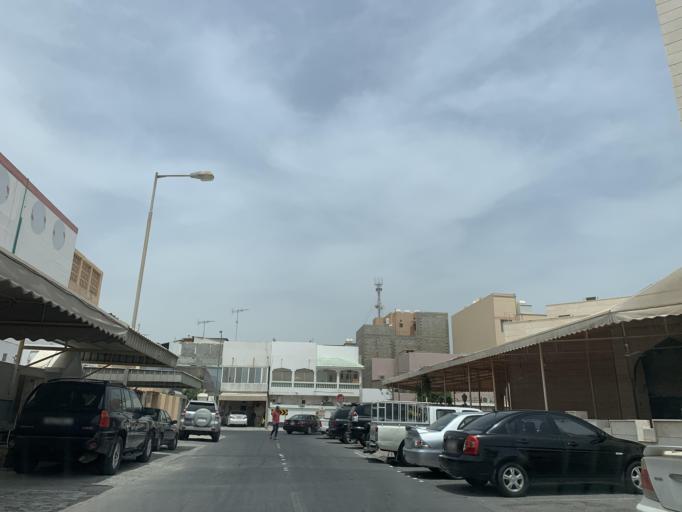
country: BH
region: Northern
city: Madinat `Isa
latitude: 26.1761
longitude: 50.5535
